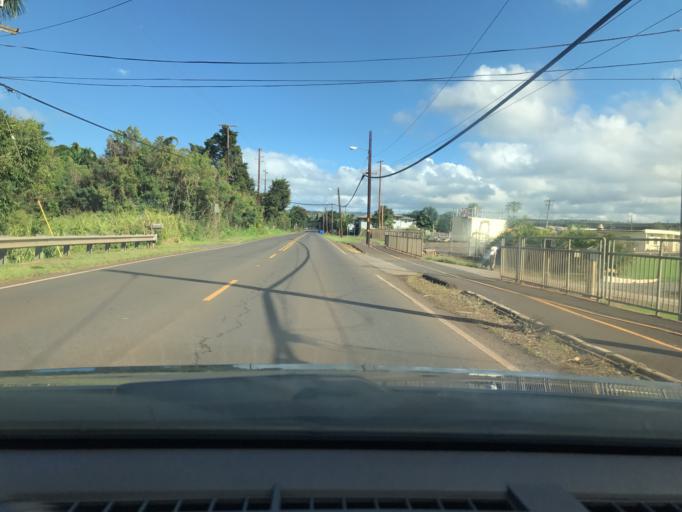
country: US
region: Hawaii
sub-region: Honolulu County
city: Hale'iwa
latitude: 21.5760
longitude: -158.1132
